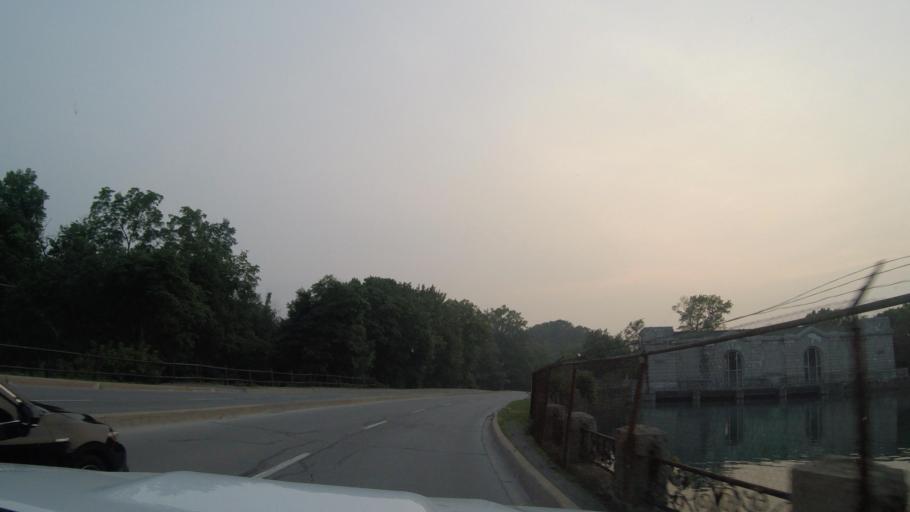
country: US
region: New York
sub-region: Niagara County
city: Niagara Falls
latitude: 43.0693
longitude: -79.0686
